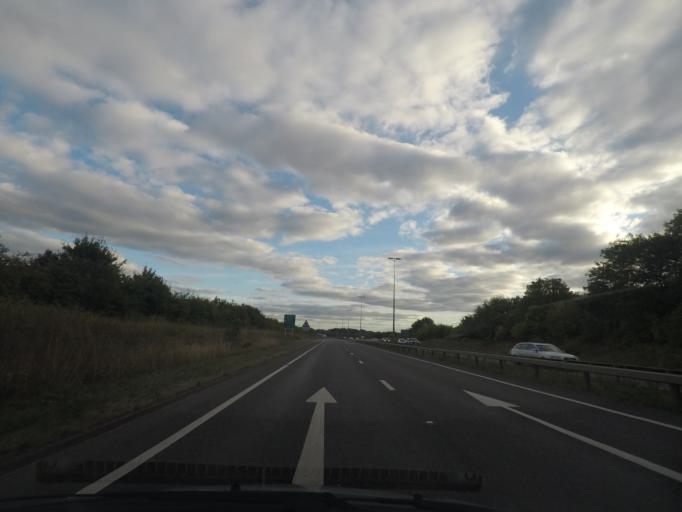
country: GB
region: England
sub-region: Oxfordshire
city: Somerton
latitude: 51.9548
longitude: -1.2035
